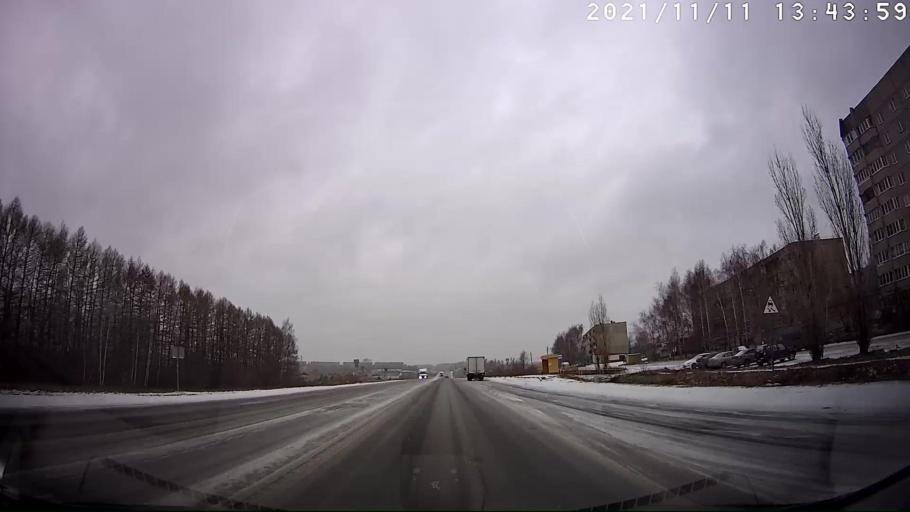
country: RU
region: Chuvashia
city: Kanash
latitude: 55.4914
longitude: 47.4767
